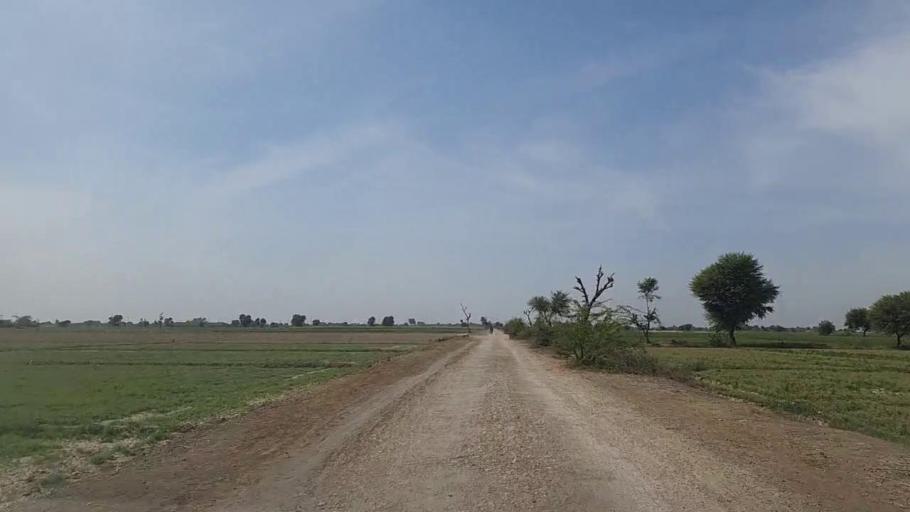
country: PK
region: Sindh
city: Samaro
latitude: 25.2128
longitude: 69.4711
